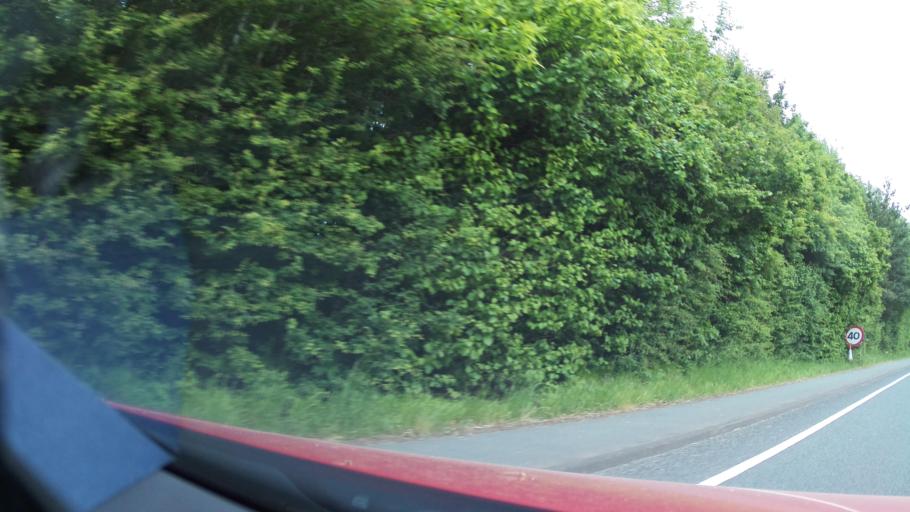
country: GB
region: England
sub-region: Worcestershire
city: Worcester
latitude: 52.1771
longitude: -2.2497
